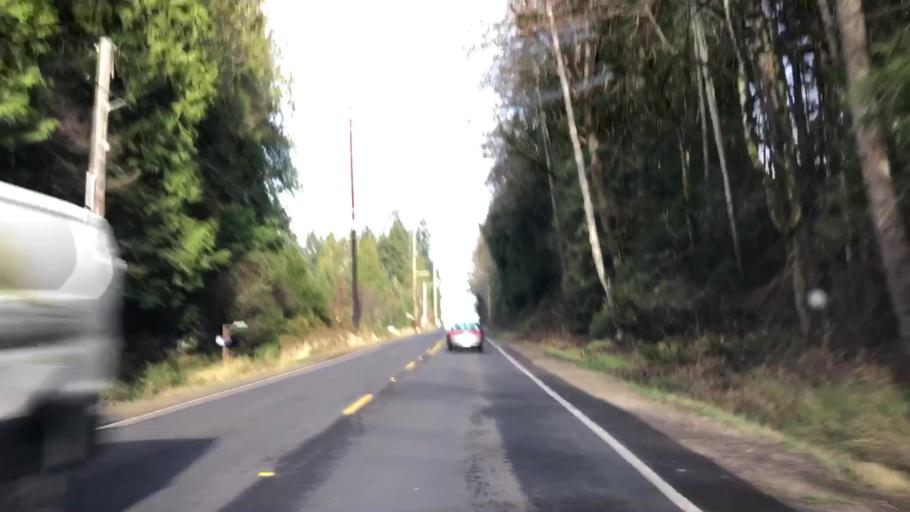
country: US
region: Washington
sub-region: Kitsap County
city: Kingston
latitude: 47.7898
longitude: -122.5414
